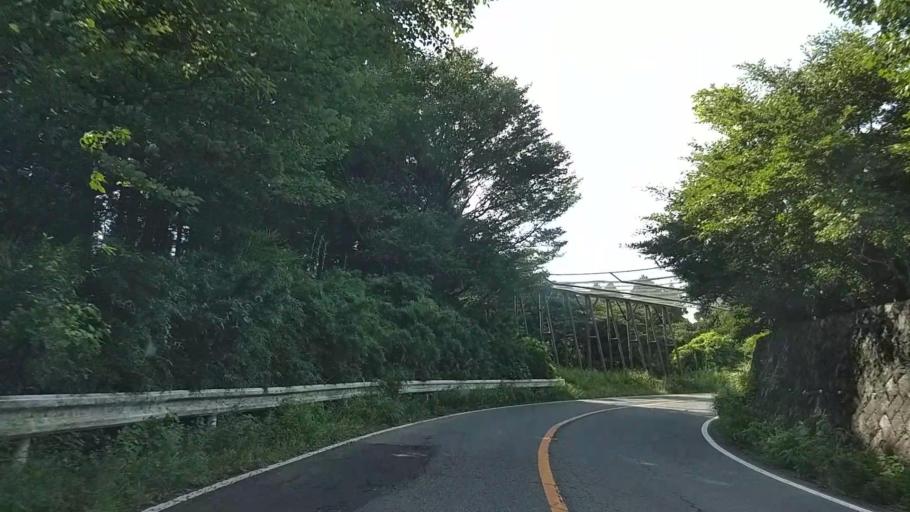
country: JP
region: Kanagawa
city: Hakone
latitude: 35.2153
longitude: 139.0135
